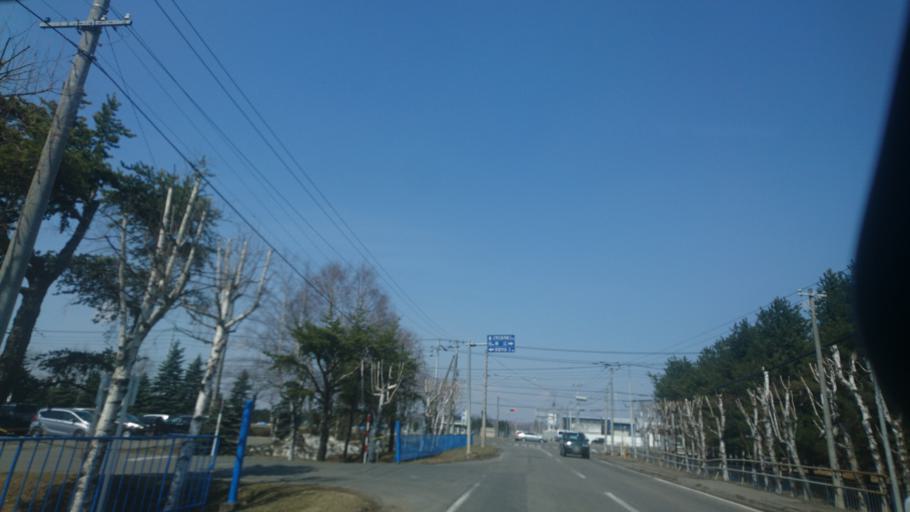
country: JP
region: Hokkaido
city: Obihiro
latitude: 42.9225
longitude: 143.0824
